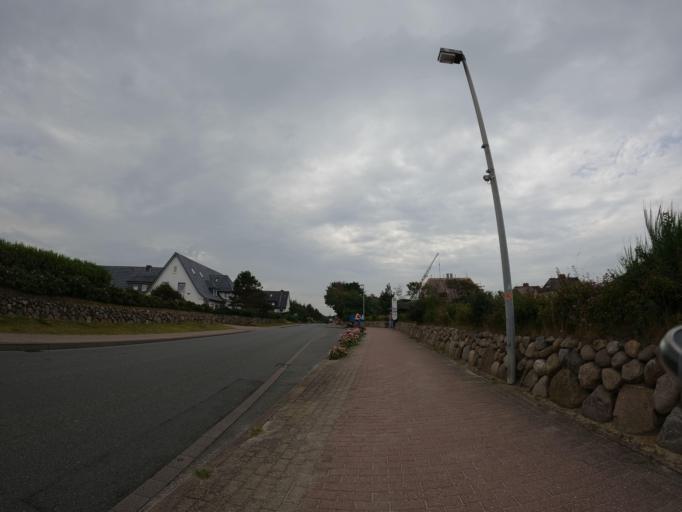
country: DE
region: Schleswig-Holstein
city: Westerland
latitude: 54.9294
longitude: 8.3187
